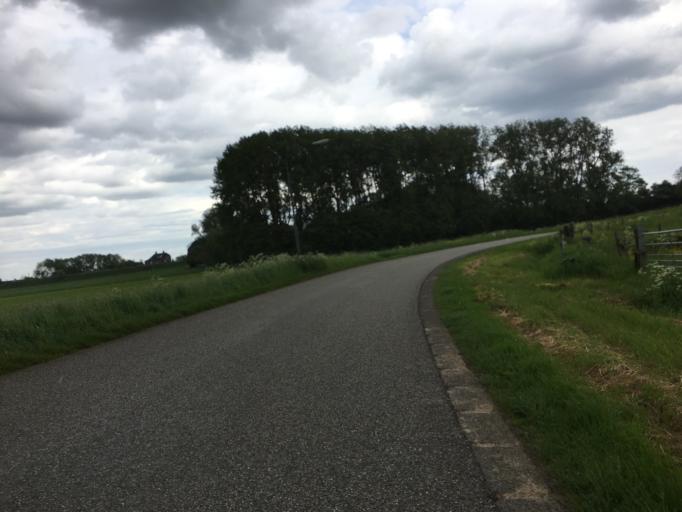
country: NL
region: Gelderland
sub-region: Gemeente Zaltbommel
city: Nederhemert-Noord
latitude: 51.7279
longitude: 5.1846
